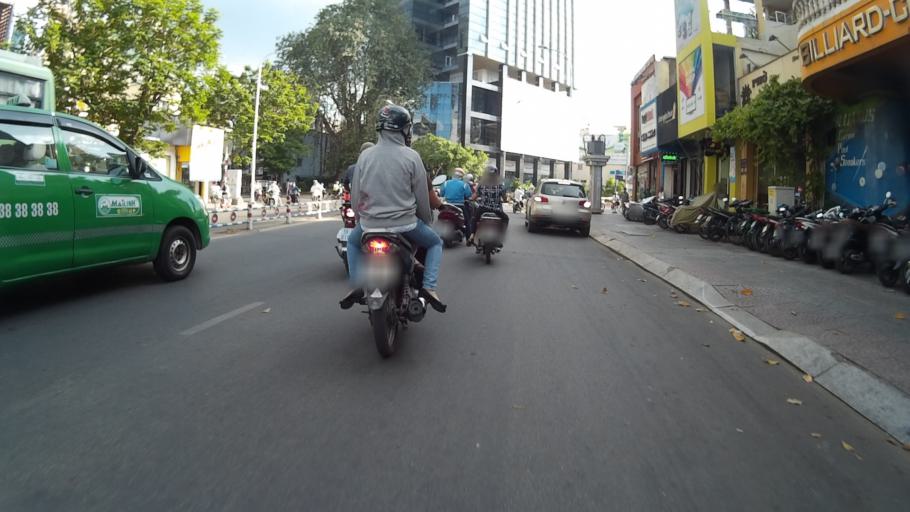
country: VN
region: Ho Chi Minh City
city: Quan Binh Thanh
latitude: 10.7922
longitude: 106.6958
